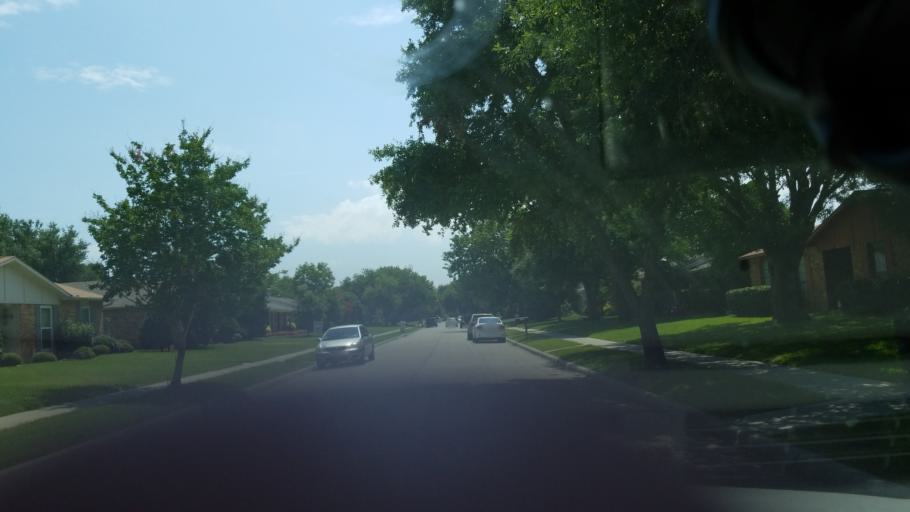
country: US
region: Texas
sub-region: Dallas County
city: Coppell
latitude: 32.9650
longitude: -96.9869
